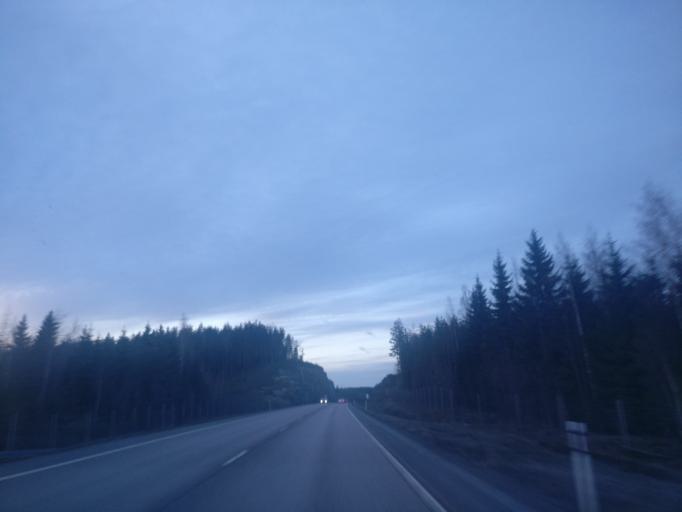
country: FI
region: Central Finland
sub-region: Jyvaeskylae
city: Saeynaetsalo
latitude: 62.2034
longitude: 25.8906
